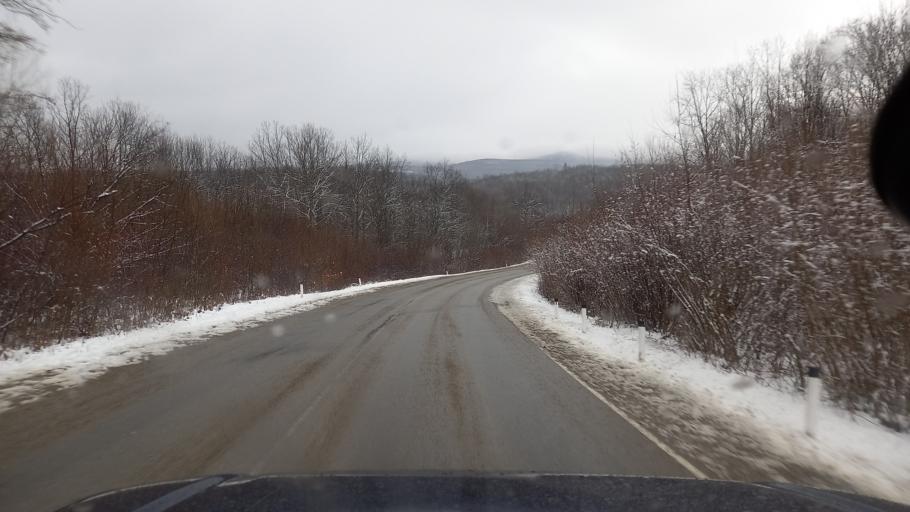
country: RU
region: Adygeya
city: Abadzekhskaya
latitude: 44.3801
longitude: 40.2472
